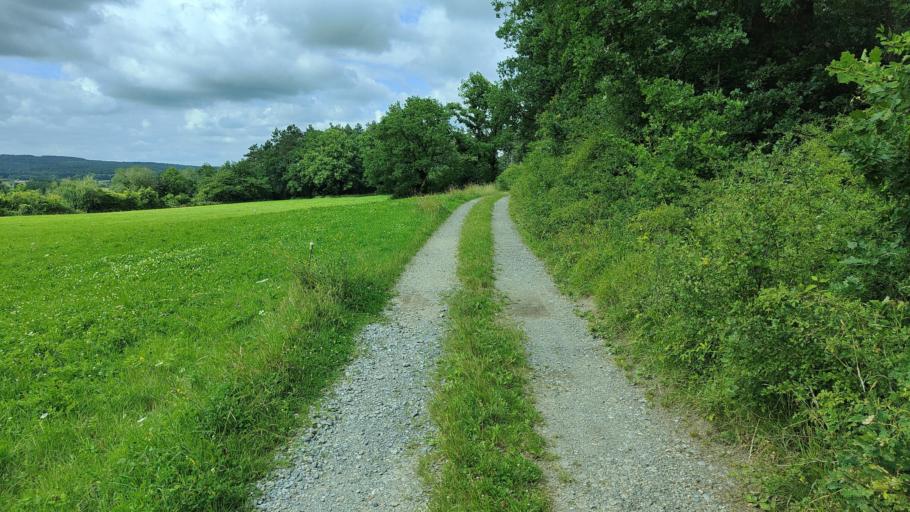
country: BE
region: Wallonia
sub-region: Province de Namur
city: Couvin
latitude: 50.0574
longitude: 4.4136
